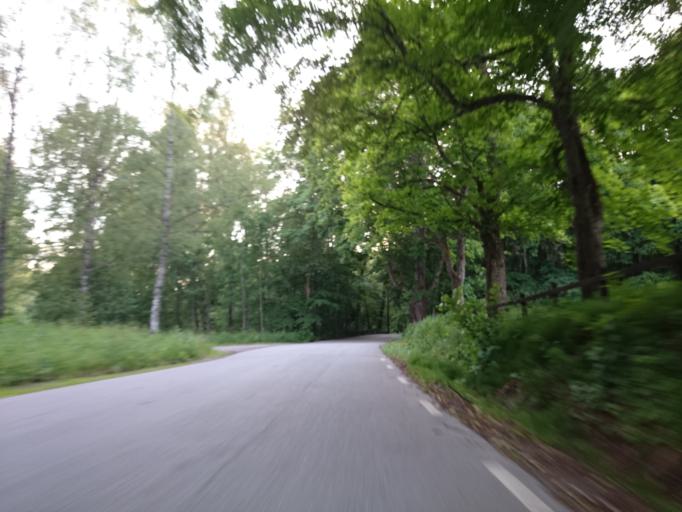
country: SE
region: Stockholm
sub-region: Botkyrka Kommun
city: Fittja
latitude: 59.2437
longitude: 17.8850
